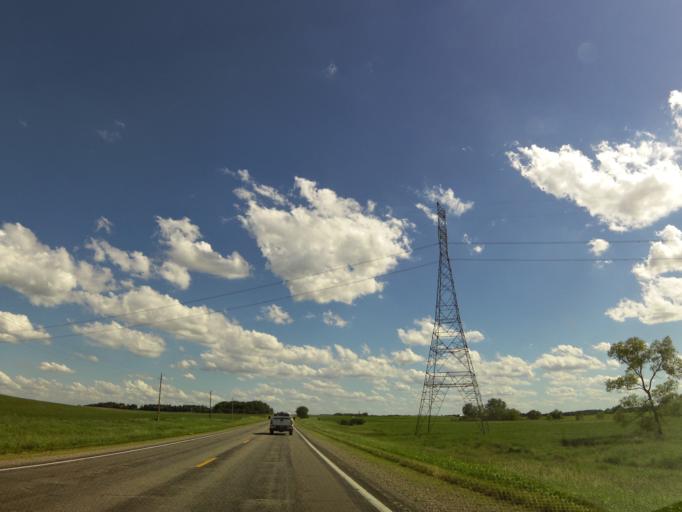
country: US
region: Minnesota
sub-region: Meeker County
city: Dassel
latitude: 45.1807
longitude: -94.3174
